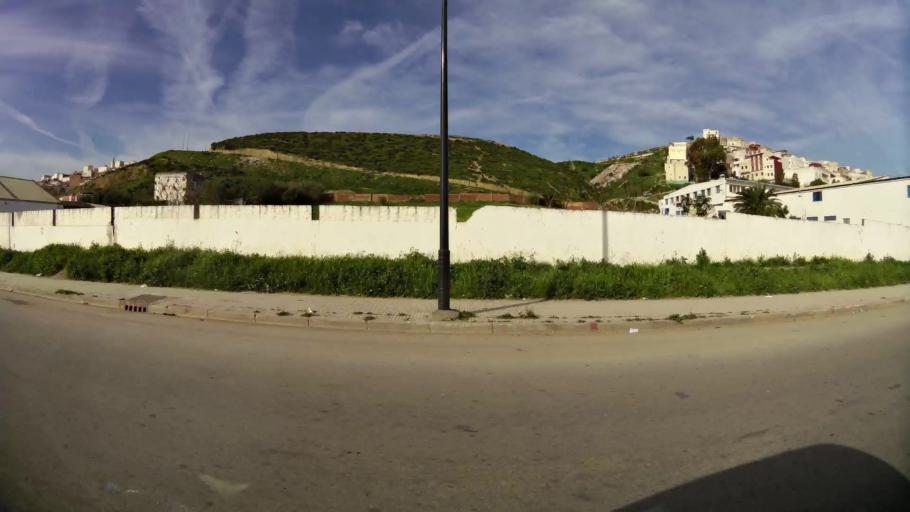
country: MA
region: Tanger-Tetouan
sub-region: Tanger-Assilah
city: Tangier
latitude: 35.7660
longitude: -5.7844
